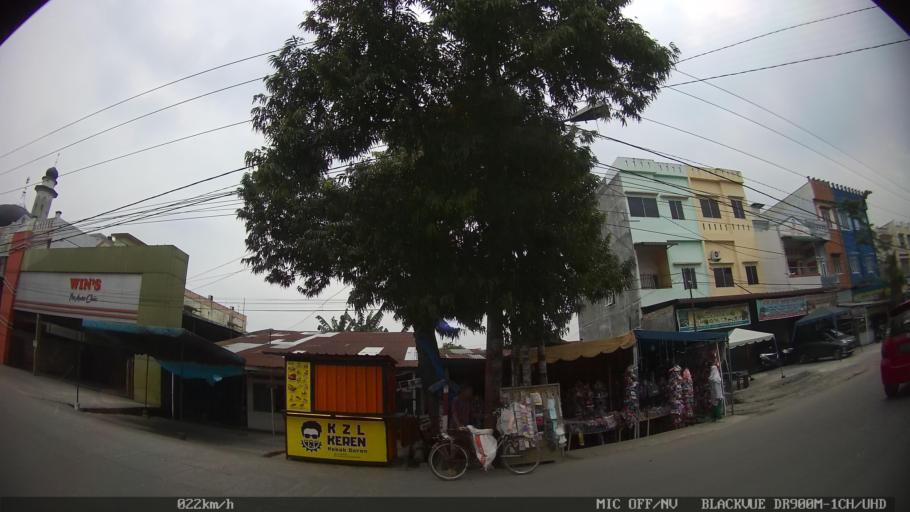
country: ID
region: North Sumatra
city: Medan
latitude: 3.5811
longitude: 98.7266
